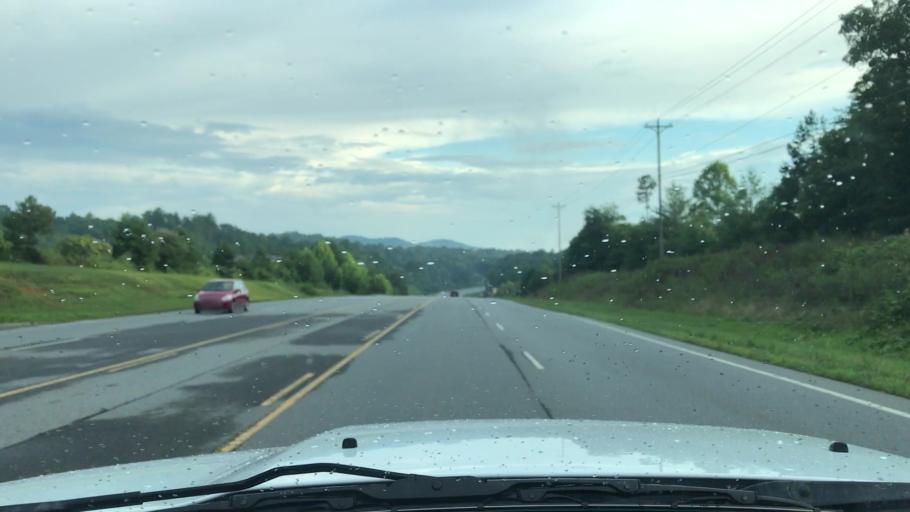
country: US
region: North Carolina
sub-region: Cherokee County
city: Murphy
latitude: 35.0199
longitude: -84.1199
